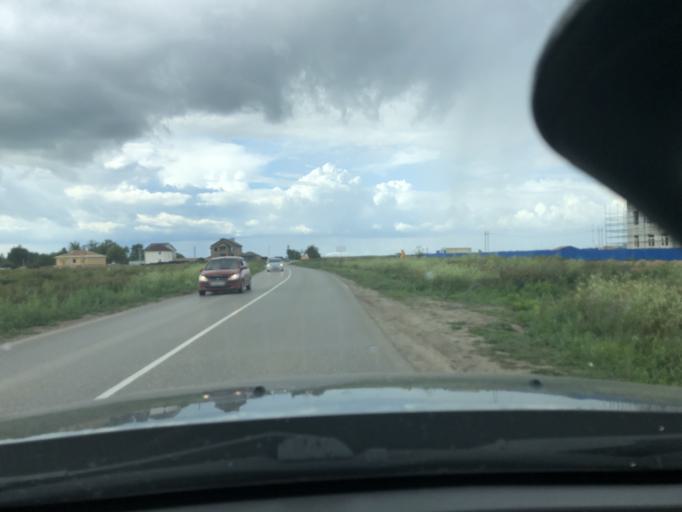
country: RU
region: Tula
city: Novomoskovsk
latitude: 54.0106
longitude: 38.2529
